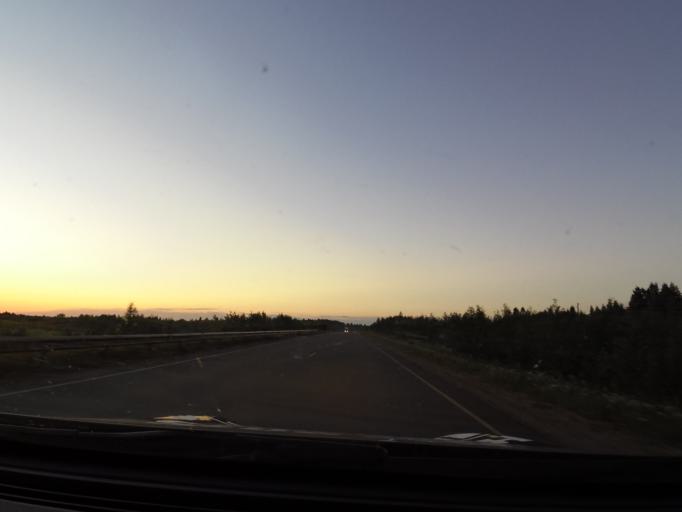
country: RU
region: Vologda
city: Vytegra
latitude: 60.9828
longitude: 36.1044
